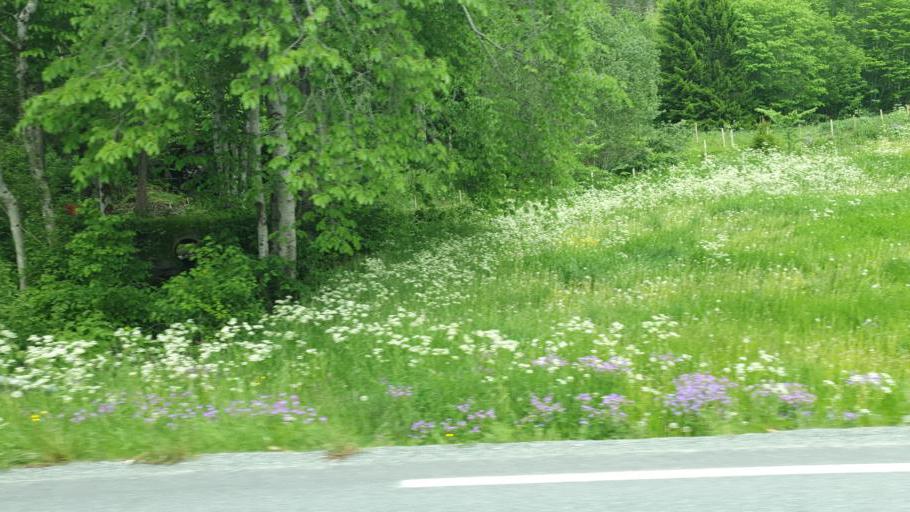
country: NO
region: Sor-Trondelag
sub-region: Trondheim
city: Trondheim
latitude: 63.5573
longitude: 10.2978
